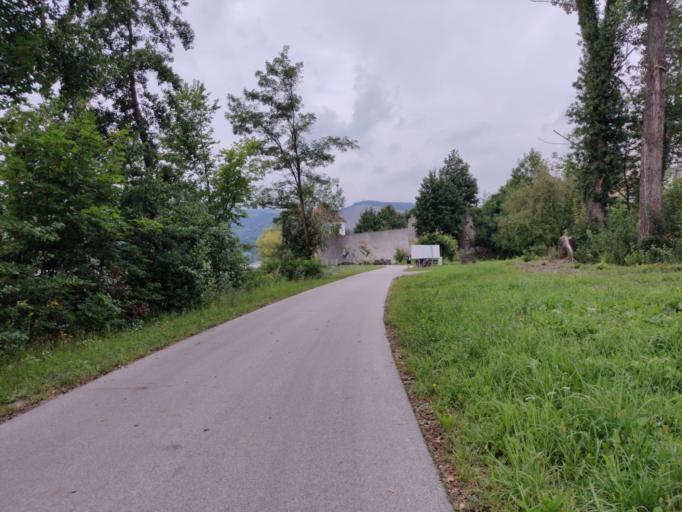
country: AT
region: Lower Austria
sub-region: Politischer Bezirk Melk
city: Ybbs an der Donau
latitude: 48.1902
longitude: 15.1145
